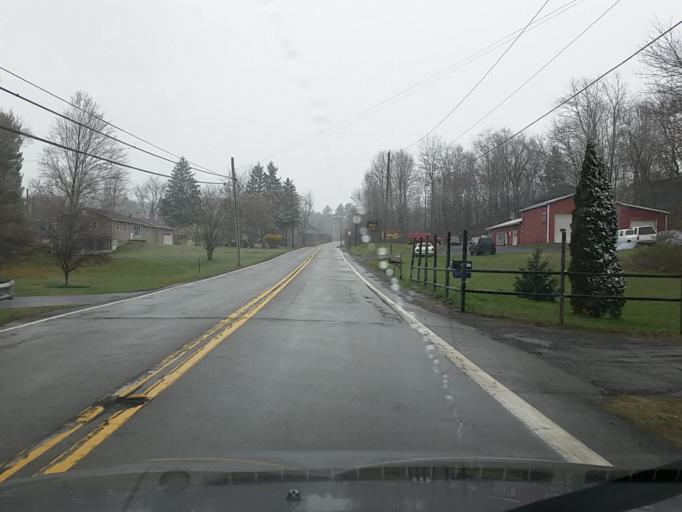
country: US
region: Pennsylvania
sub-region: Luzerne County
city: East Berwick
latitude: 41.1917
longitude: -76.2740
